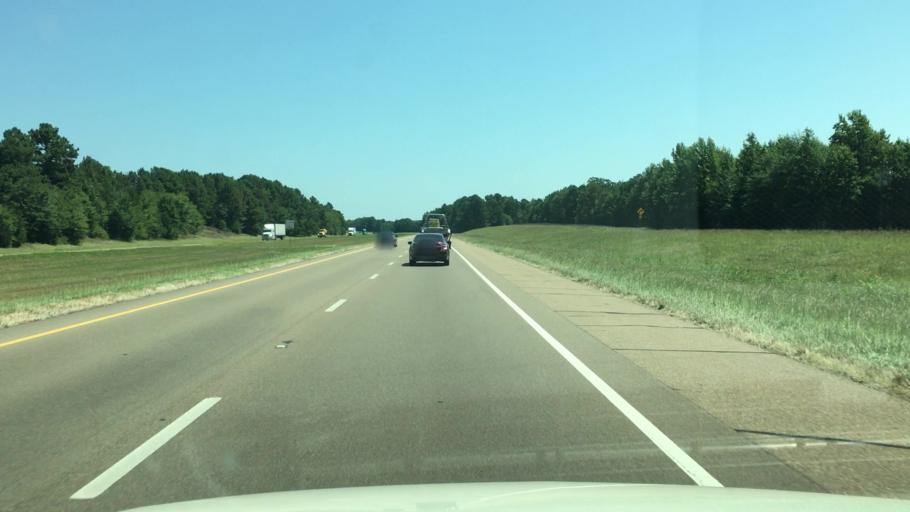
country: US
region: Texas
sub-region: Bowie County
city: De Kalb
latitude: 33.3879
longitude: -94.5963
